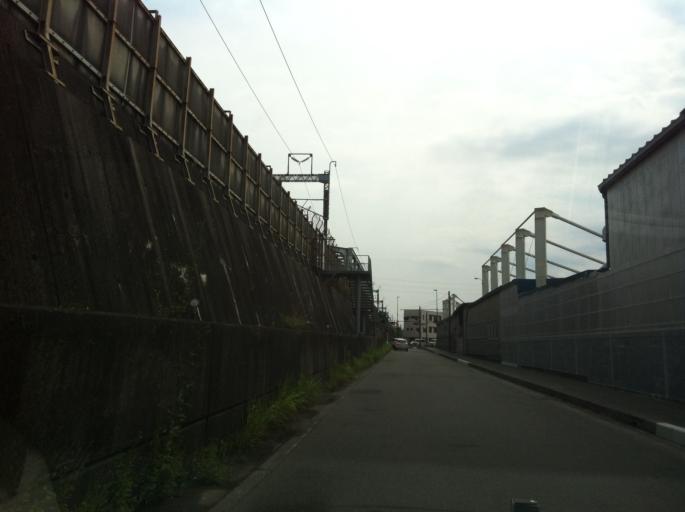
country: JP
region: Shizuoka
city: Shizuoka-shi
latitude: 35.0170
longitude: 138.4617
